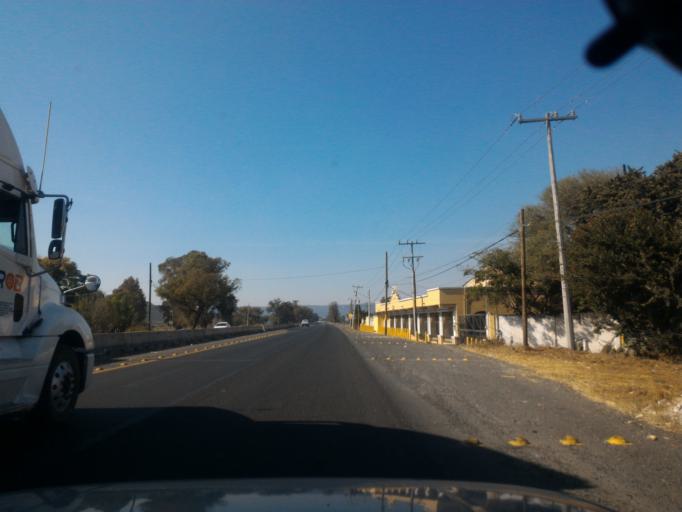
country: MX
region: Jalisco
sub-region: Poncitlan
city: Cuitzeo (La Estancia)
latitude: 20.3543
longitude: -102.7974
